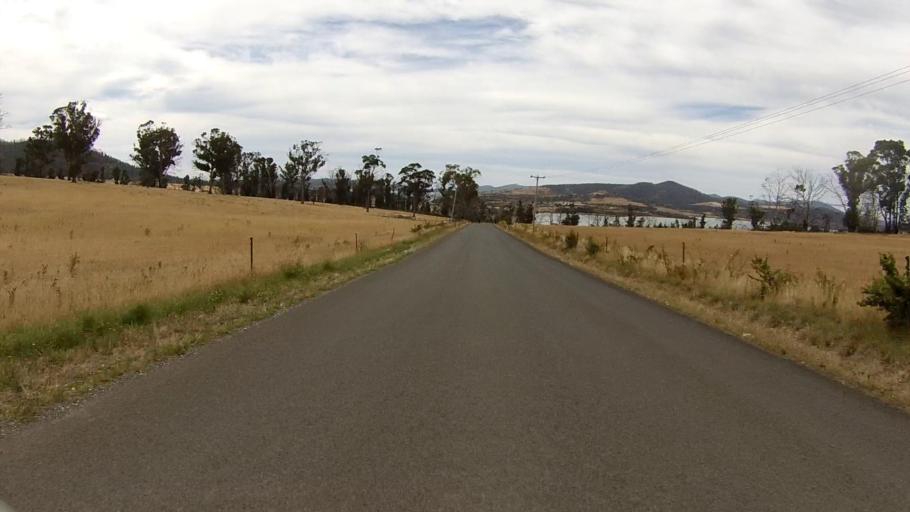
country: AU
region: Tasmania
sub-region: Sorell
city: Sorell
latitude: -42.8914
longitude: 147.7840
